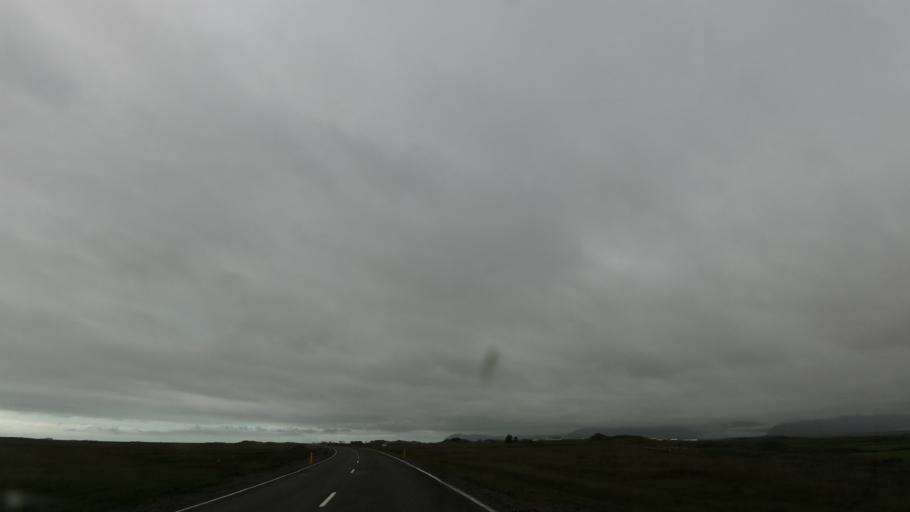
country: IS
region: East
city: Hoefn
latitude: 64.2879
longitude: -15.4598
